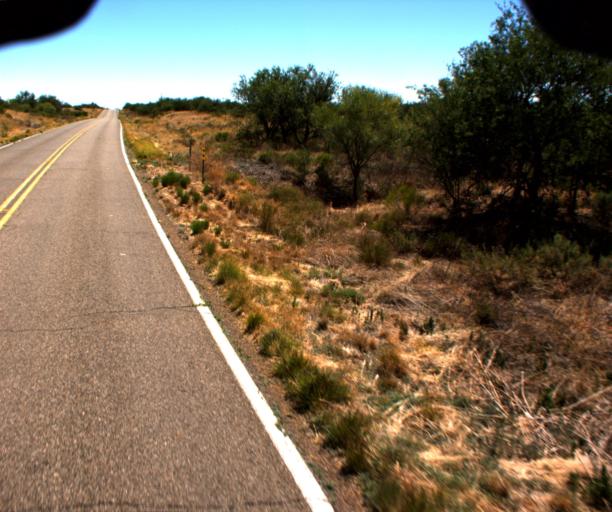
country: US
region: Arizona
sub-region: Pima County
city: Arivaca Junction
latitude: 31.6565
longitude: -111.4931
